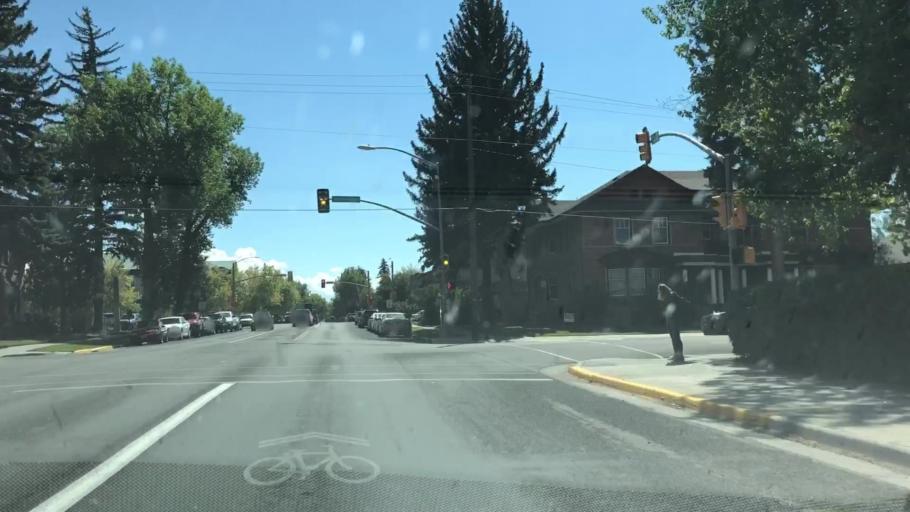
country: US
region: Wyoming
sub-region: Albany County
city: Laramie
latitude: 41.3117
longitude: -105.5856
